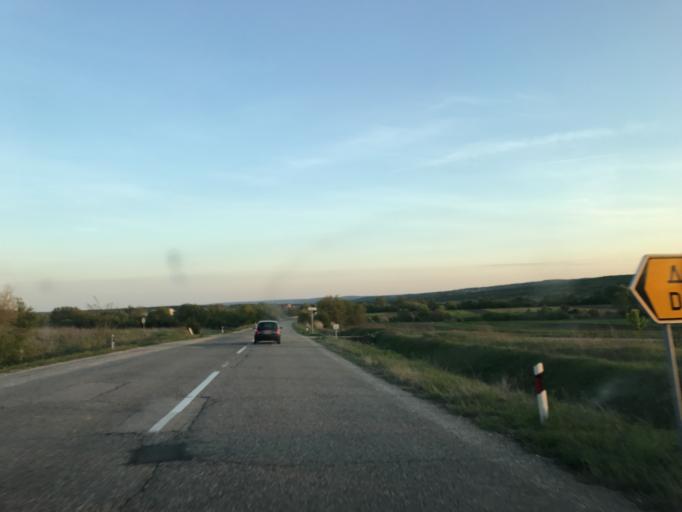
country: RO
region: Mehedinti
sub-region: Comuna Gogosu
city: Ostrovu Mare
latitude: 44.3026
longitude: 22.5068
